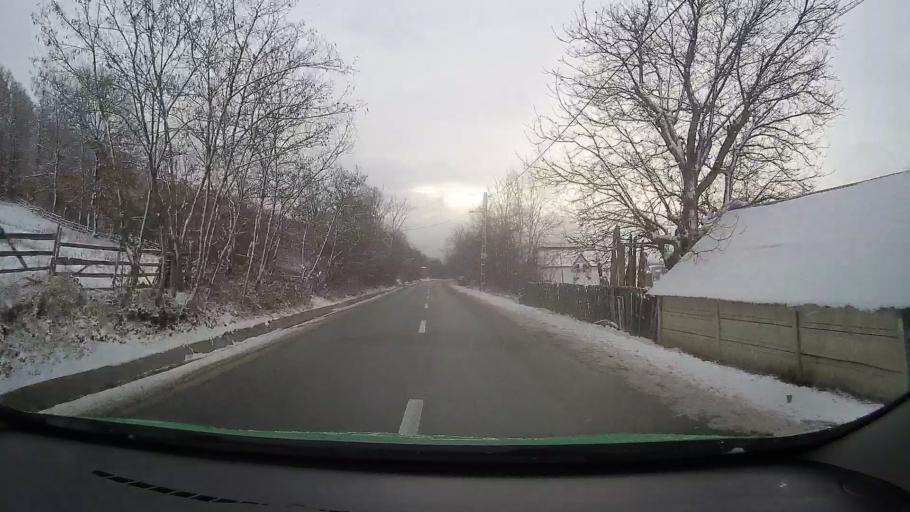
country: RO
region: Hunedoara
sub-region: Oras Hateg
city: Hateg
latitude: 45.6303
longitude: 22.9302
